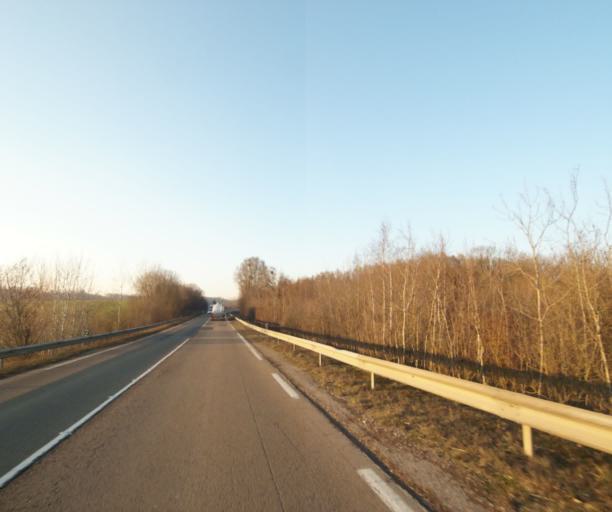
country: FR
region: Champagne-Ardenne
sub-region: Departement de la Haute-Marne
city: Bienville
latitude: 48.5786
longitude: 5.0331
